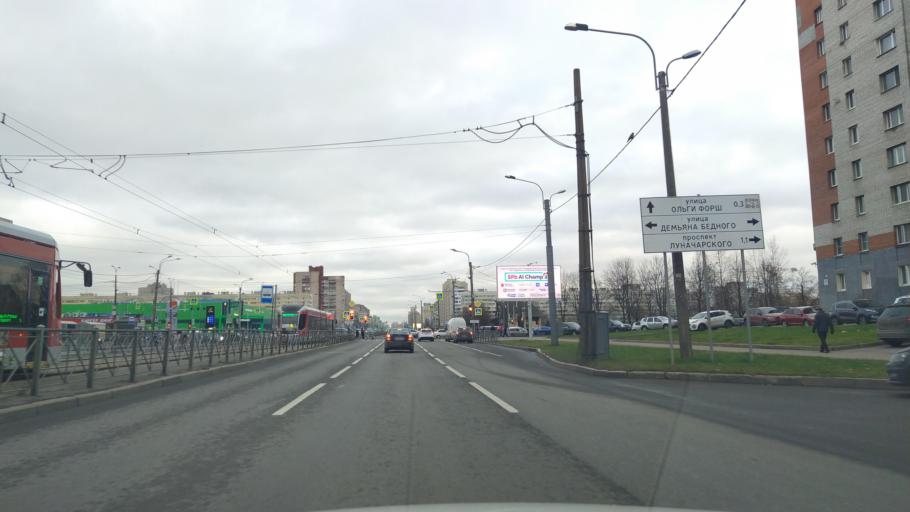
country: RU
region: St.-Petersburg
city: Grazhdanka
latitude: 60.0426
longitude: 30.3844
